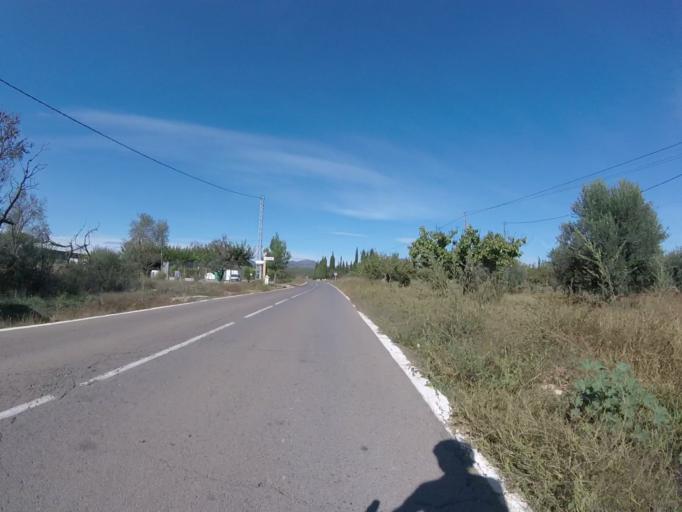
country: ES
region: Valencia
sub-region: Provincia de Castello
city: Benlloch
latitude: 40.2134
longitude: 0.0219
